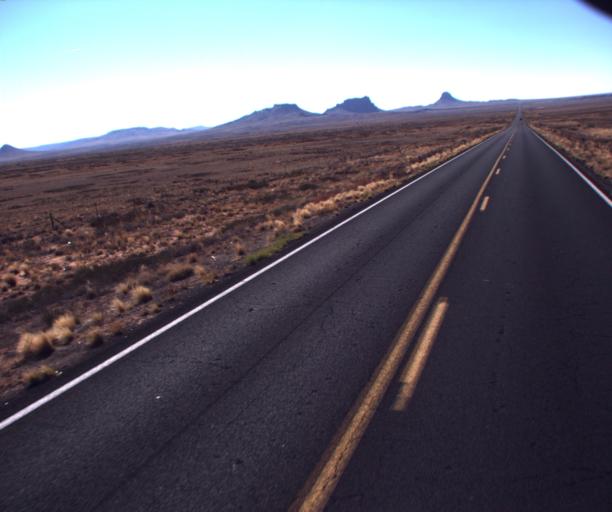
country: US
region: Arizona
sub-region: Navajo County
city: Dilkon
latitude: 35.3928
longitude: -110.4259
